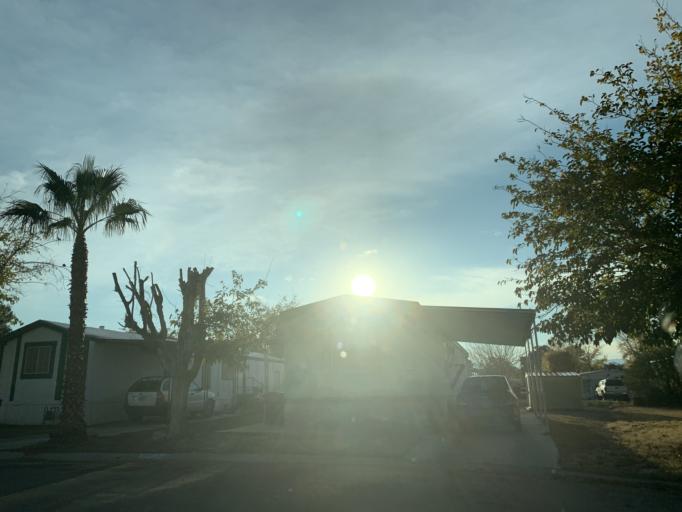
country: US
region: Nevada
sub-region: Clark County
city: Spring Valley
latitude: 36.1035
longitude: -115.2187
